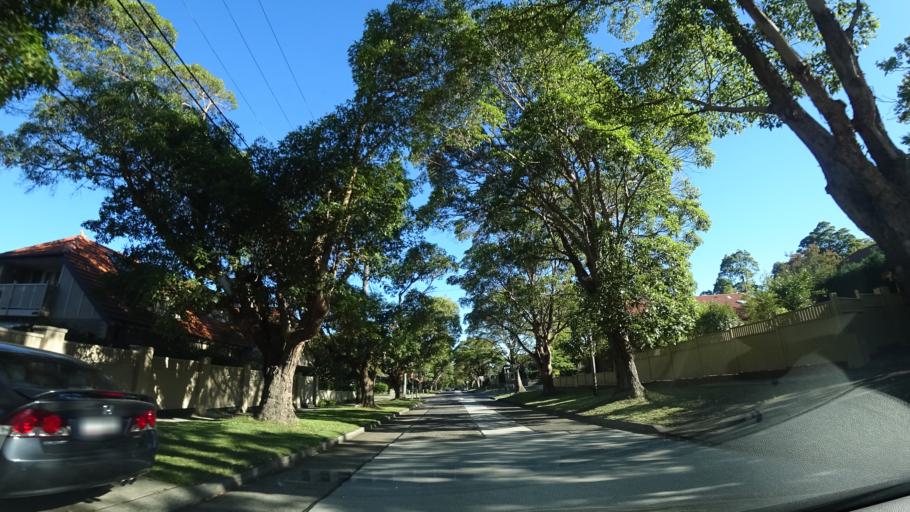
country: AU
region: New South Wales
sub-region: Ku-ring-gai
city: Roseville Chase
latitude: -33.7875
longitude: 151.1894
